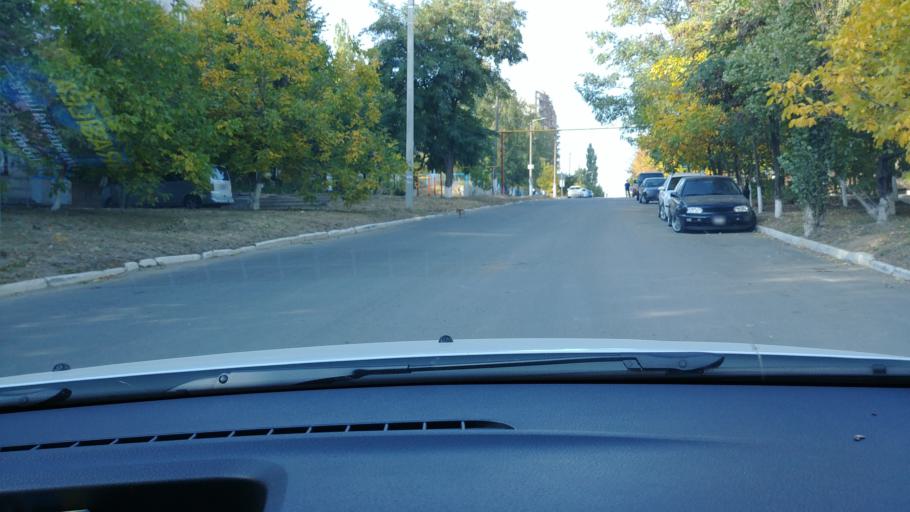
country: MD
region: Rezina
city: Rezina
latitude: 47.7461
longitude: 28.9561
